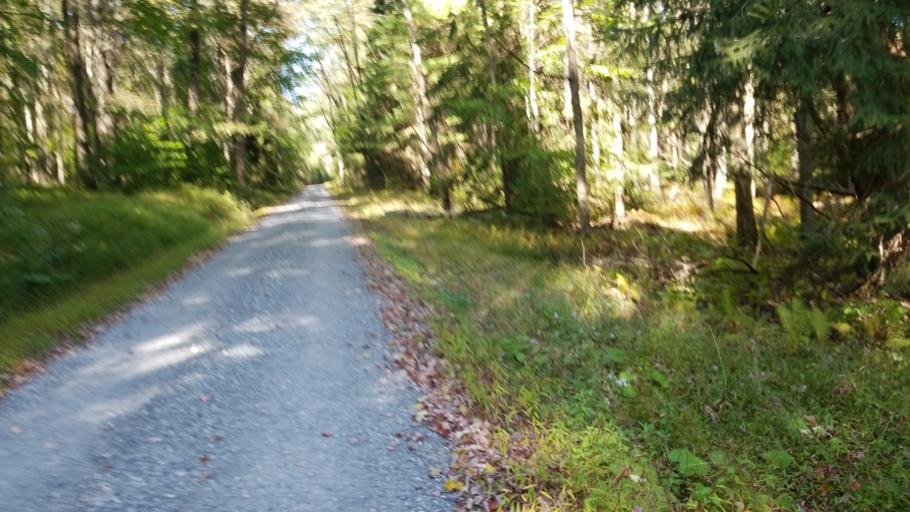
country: US
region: Pennsylvania
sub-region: Clearfield County
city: Clearfield
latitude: 41.1878
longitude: -78.5147
